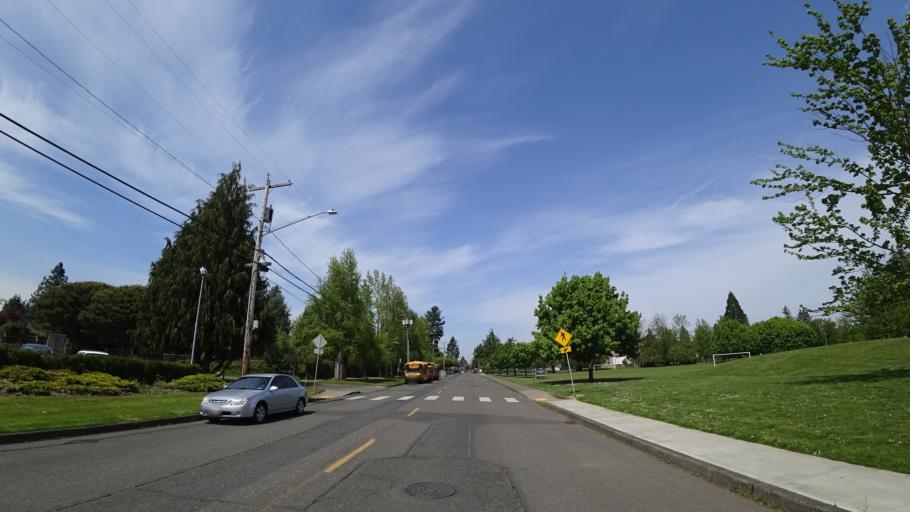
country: US
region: Oregon
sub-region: Multnomah County
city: Lents
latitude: 45.4735
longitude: -122.6022
